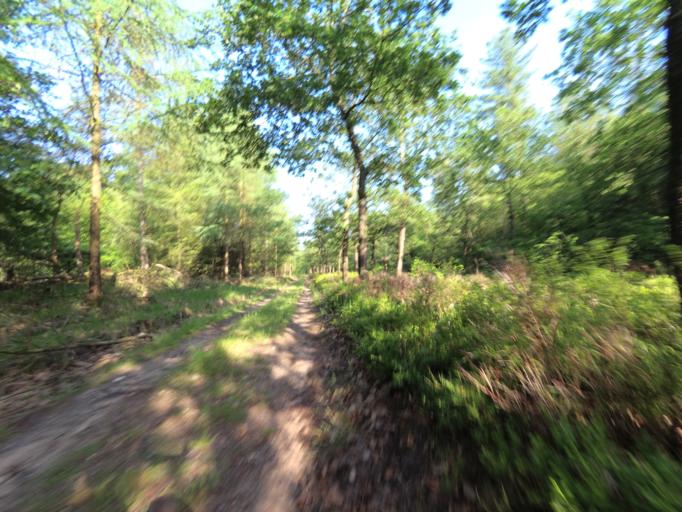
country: NL
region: Gelderland
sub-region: Gemeente Apeldoorn
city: Beekbergen
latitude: 52.1527
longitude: 5.8928
